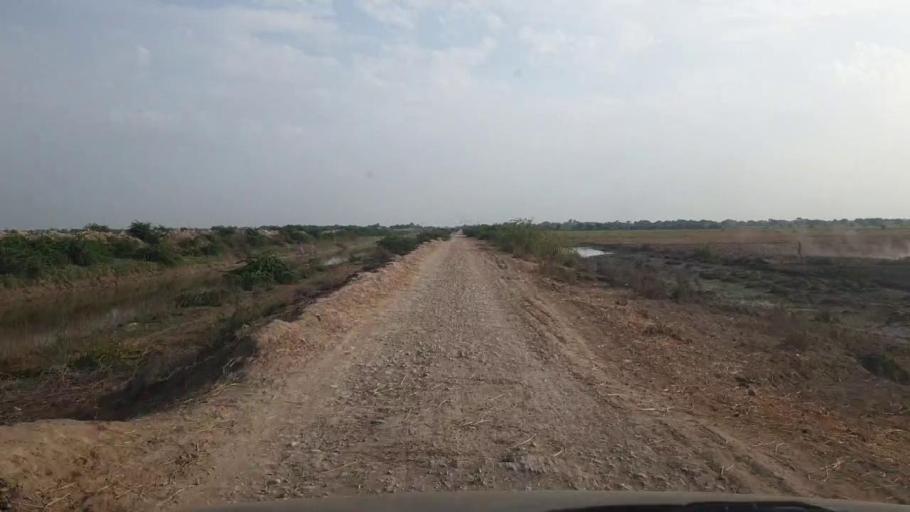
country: PK
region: Sindh
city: Badin
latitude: 24.5569
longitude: 68.6694
